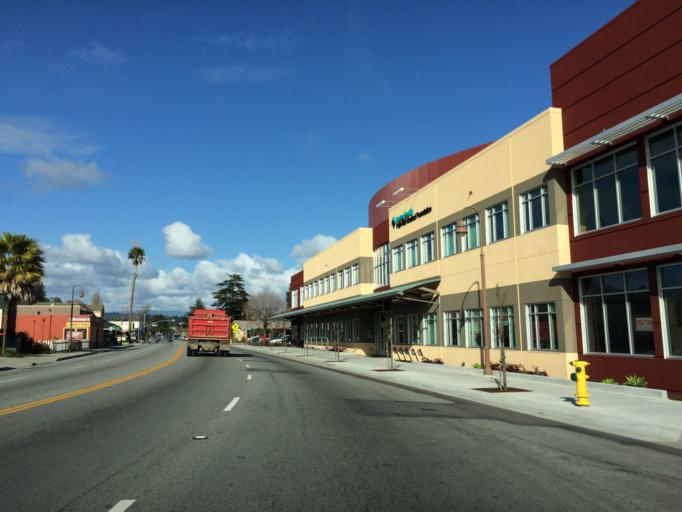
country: US
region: California
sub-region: Santa Cruz County
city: Santa Cruz
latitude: 36.9677
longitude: -122.0387
